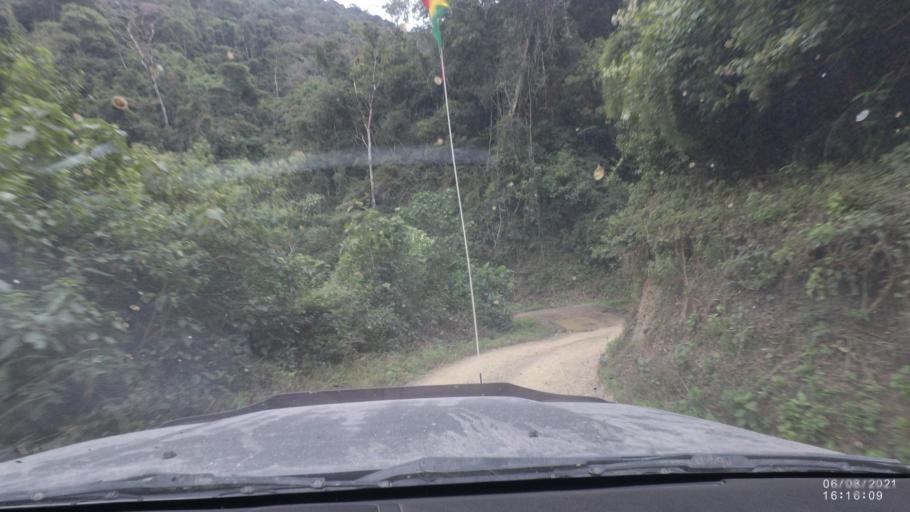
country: BO
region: La Paz
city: Quime
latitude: -16.5501
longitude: -66.7367
